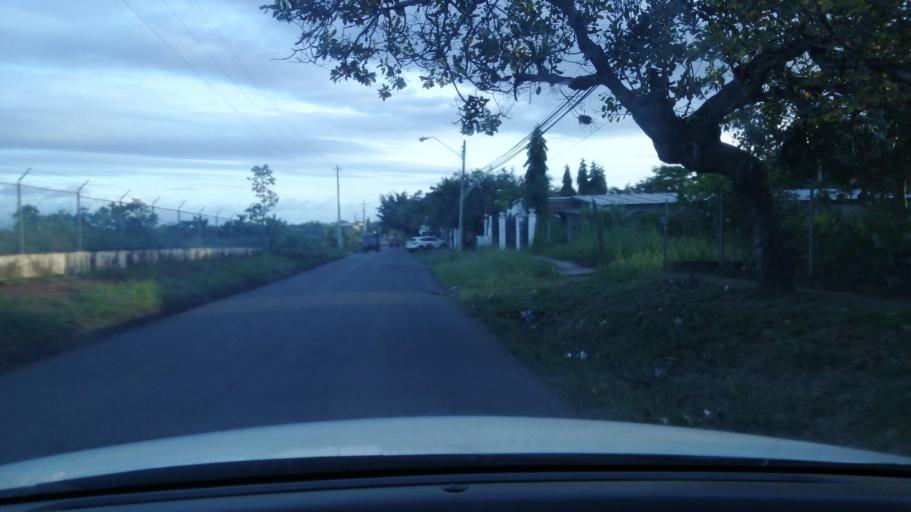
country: PA
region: Chiriqui
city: David
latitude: 8.4069
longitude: -82.4347
